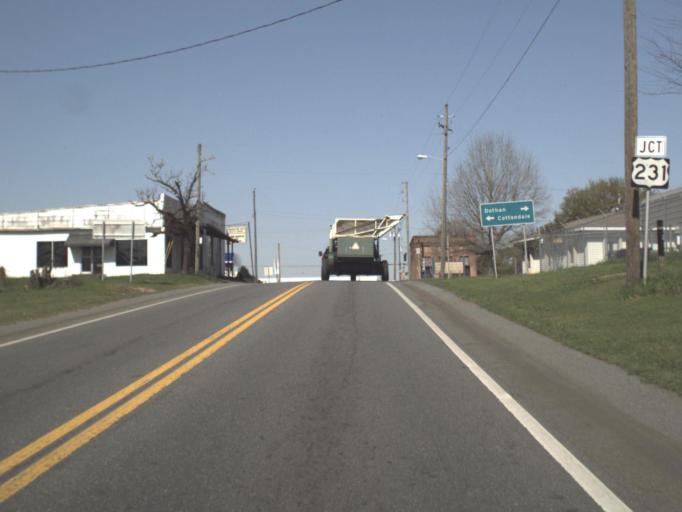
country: US
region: Florida
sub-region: Jackson County
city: Graceville
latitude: 30.9501
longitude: -85.4007
